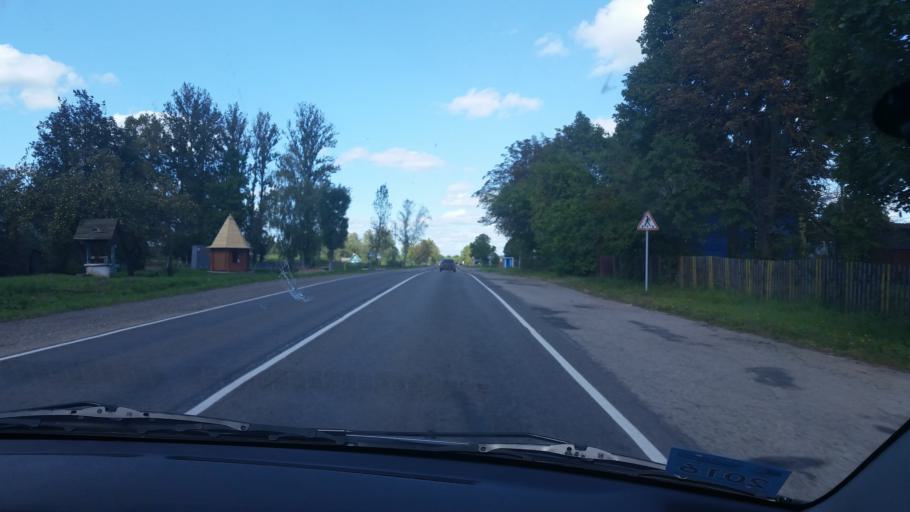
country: BY
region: Vitebsk
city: Vitebsk
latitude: 55.1109
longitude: 30.2830
